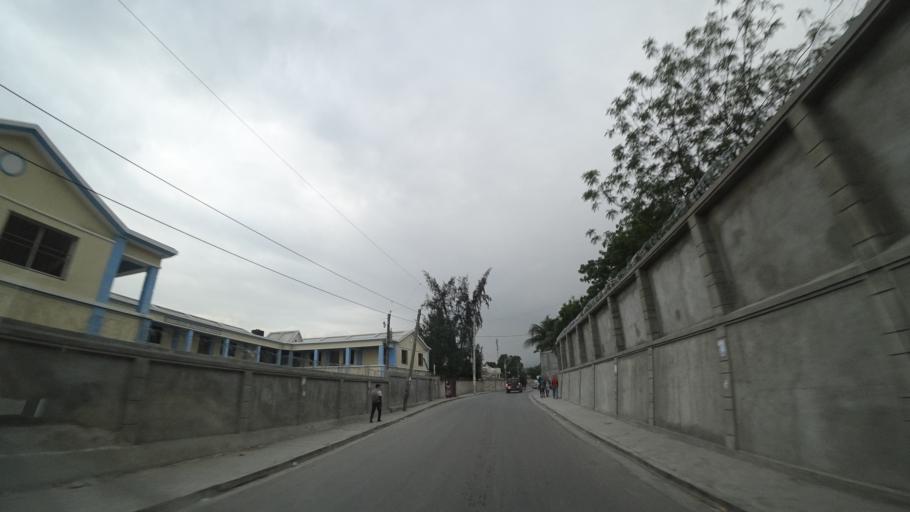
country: HT
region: Ouest
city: Delmas 73
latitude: 18.5649
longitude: -72.2973
